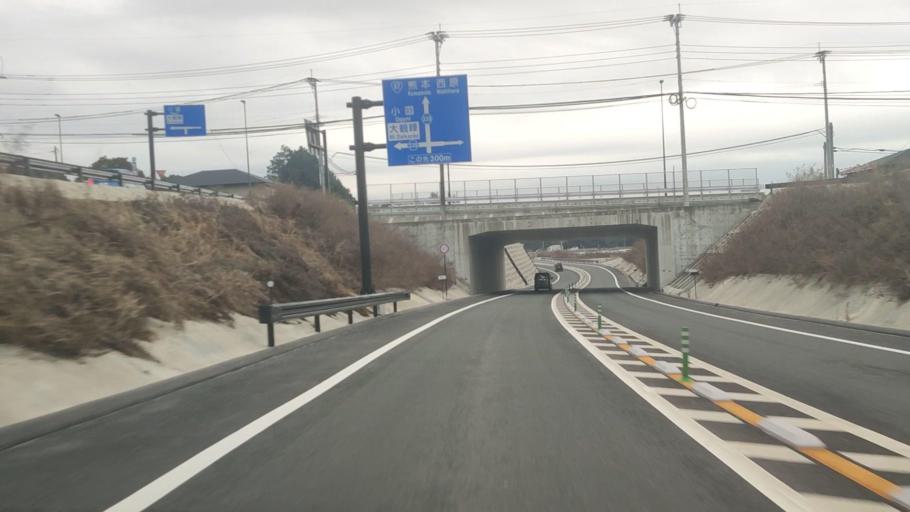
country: JP
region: Kumamoto
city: Ozu
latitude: 32.8908
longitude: 130.8964
